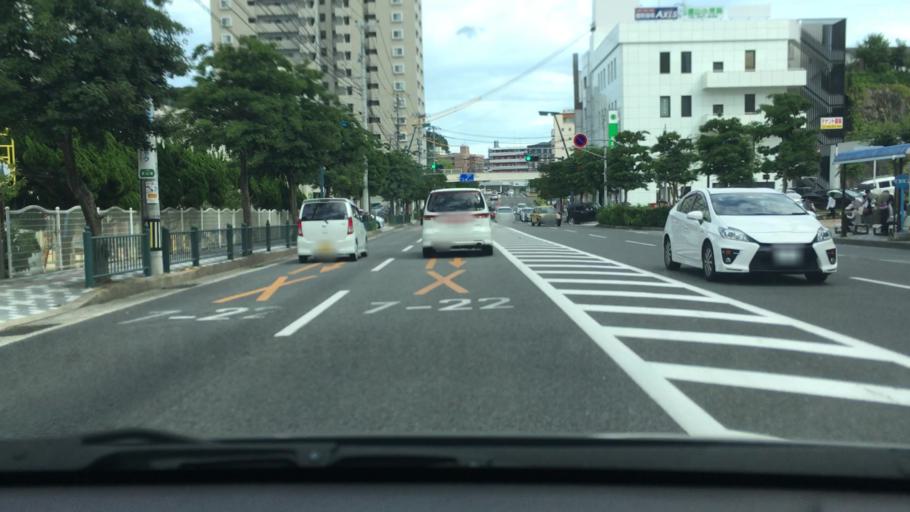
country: JP
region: Nagasaki
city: Togitsu
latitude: 32.8041
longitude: 129.8513
